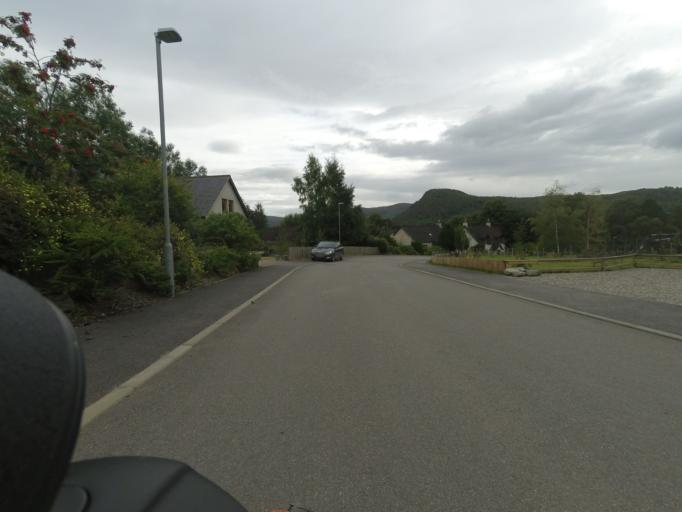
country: GB
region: Scotland
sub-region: Highland
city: Muir of Ord
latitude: 57.5695
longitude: -4.5777
